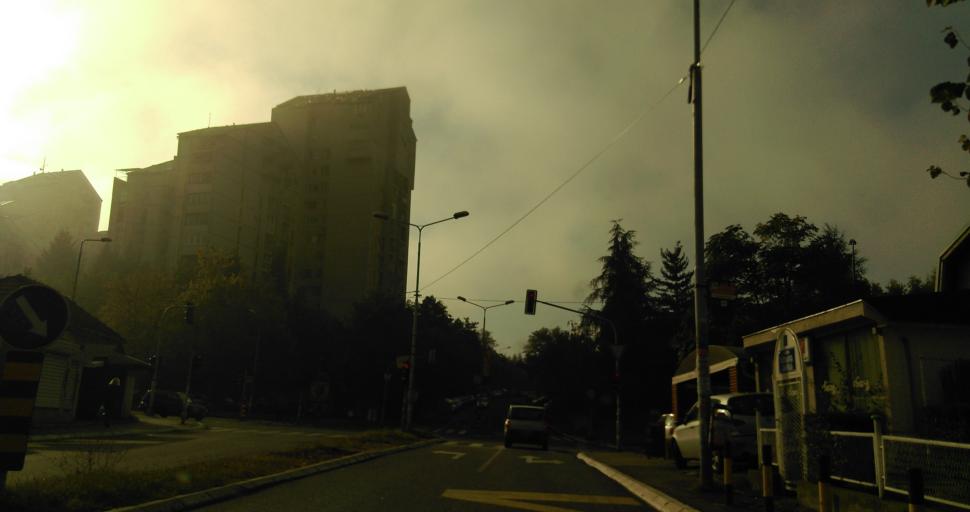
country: RS
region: Central Serbia
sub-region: Belgrade
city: Rakovica
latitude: 44.7310
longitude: 20.4211
